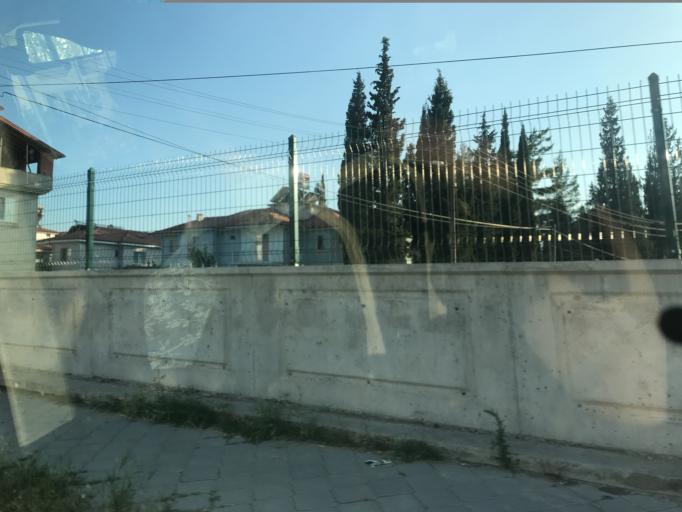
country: TR
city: Dalyan
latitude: 36.9698
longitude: 28.6872
